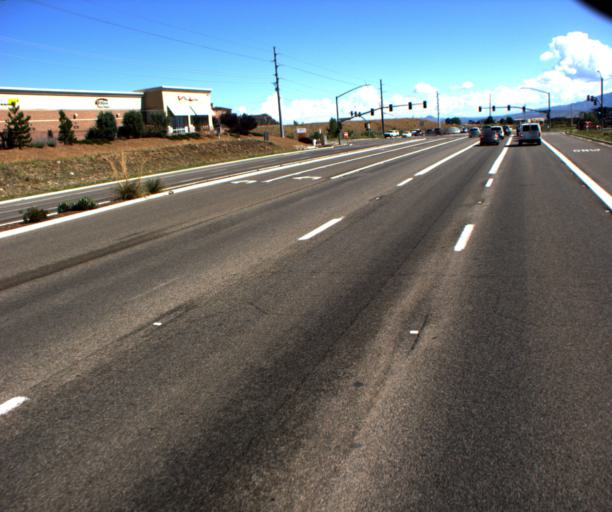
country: US
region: Arizona
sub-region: Yavapai County
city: Prescott Valley
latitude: 34.5753
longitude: -112.3661
